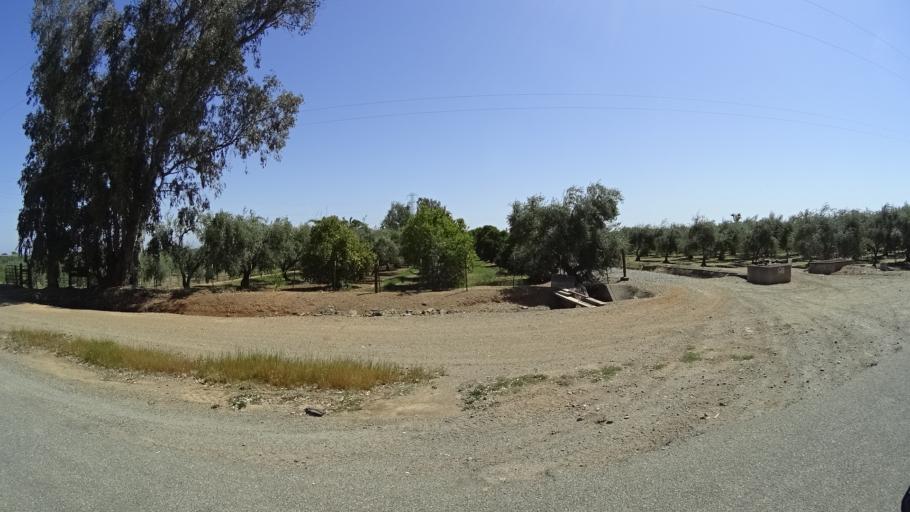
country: US
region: California
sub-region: Glenn County
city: Orland
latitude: 39.7923
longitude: -122.1691
